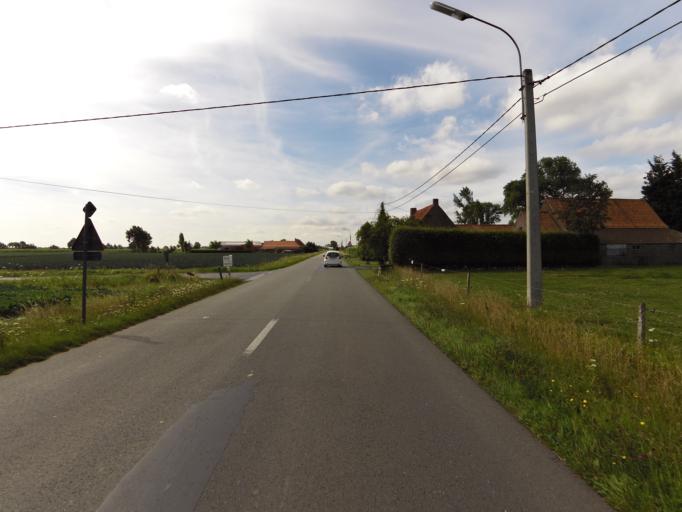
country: BE
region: Flanders
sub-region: Provincie West-Vlaanderen
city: Houthulst
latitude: 50.9464
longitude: 2.9409
